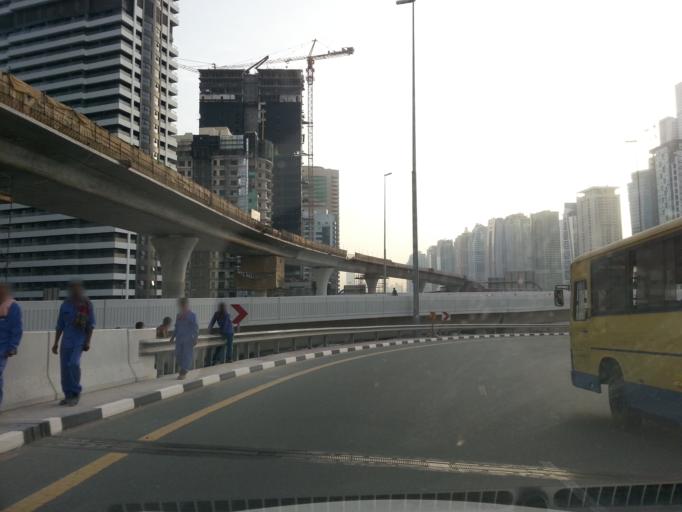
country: AE
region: Dubai
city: Dubai
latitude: 25.0668
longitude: 55.1326
